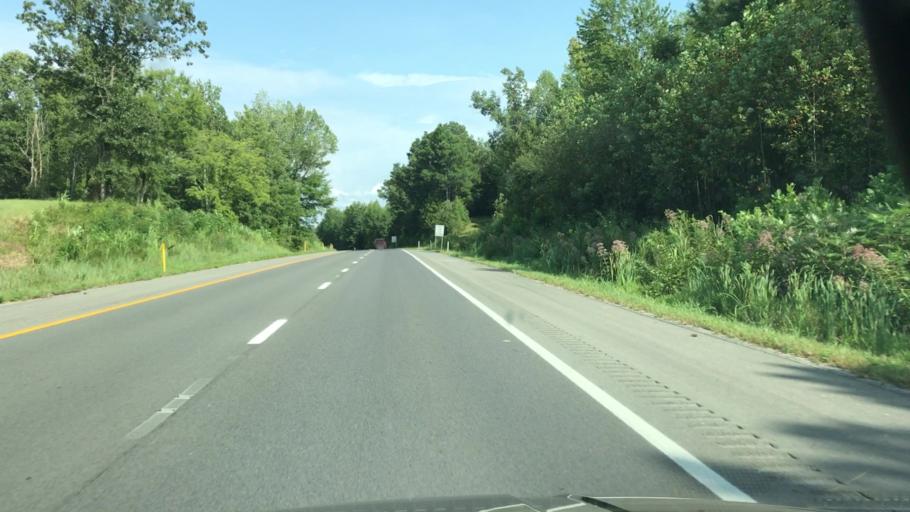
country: US
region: Kentucky
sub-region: Hopkins County
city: Nortonville
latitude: 37.2114
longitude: -87.4243
